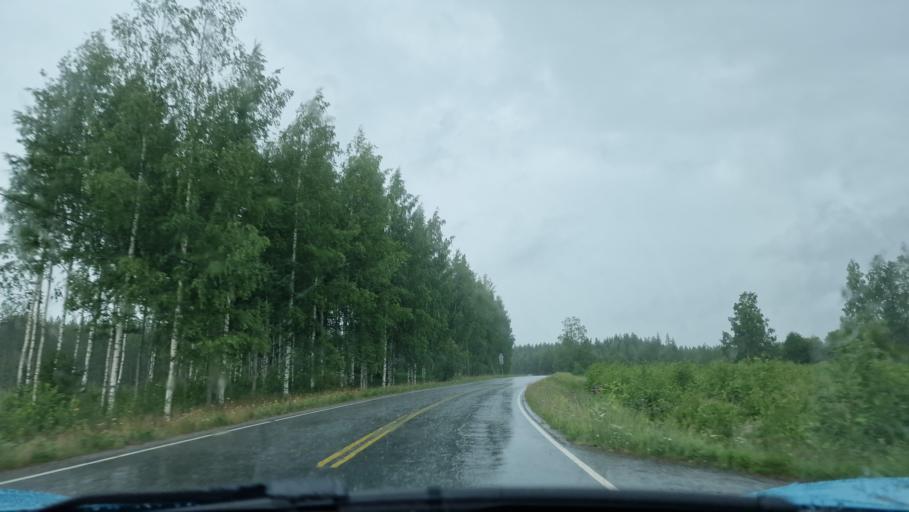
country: FI
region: Southern Ostrobothnia
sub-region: Jaerviseutu
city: Soini
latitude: 62.8294
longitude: 24.3394
